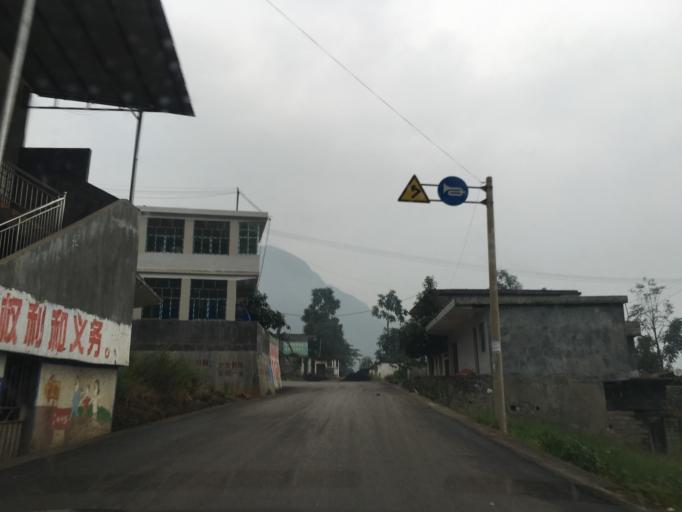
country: CN
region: Guizhou Sheng
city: Liupanshui
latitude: 26.0639
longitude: 105.1356
